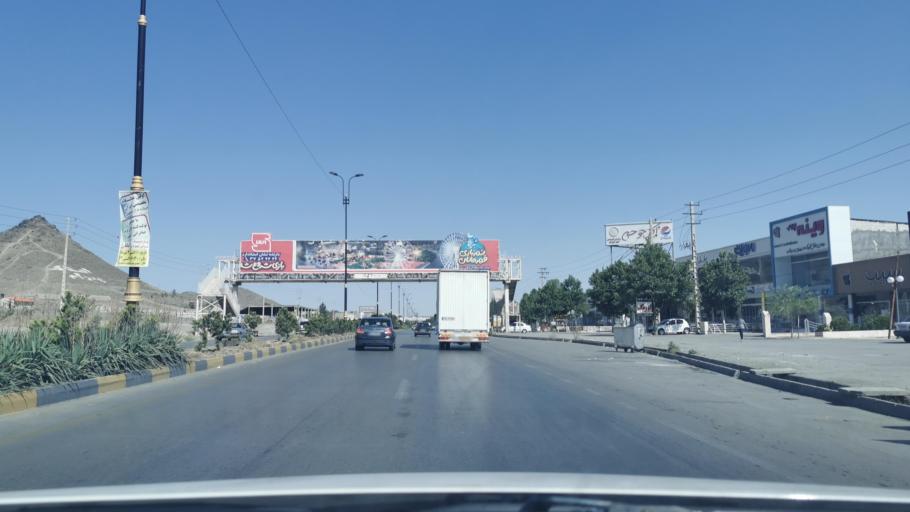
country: IR
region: Razavi Khorasan
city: Torqabeh
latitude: 36.3929
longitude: 59.4017
